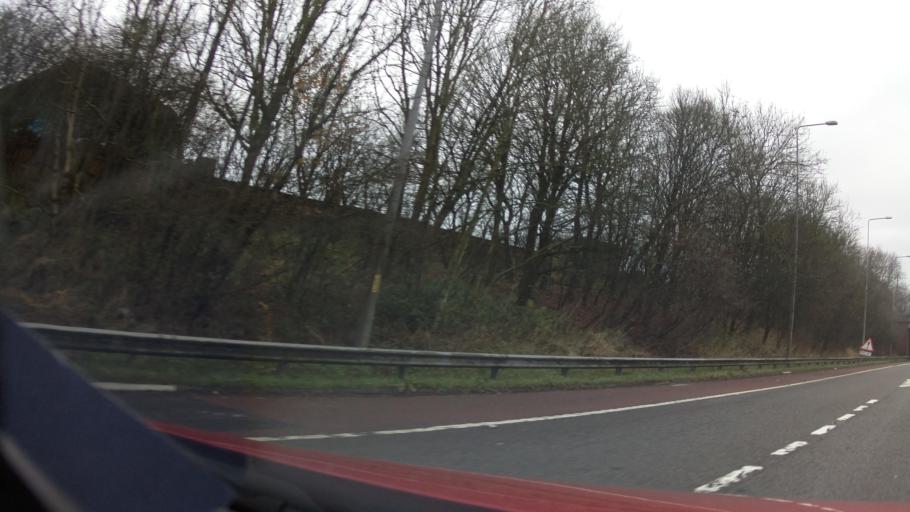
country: GB
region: England
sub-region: Lancashire
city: Coppull
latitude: 53.6281
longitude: -2.6895
